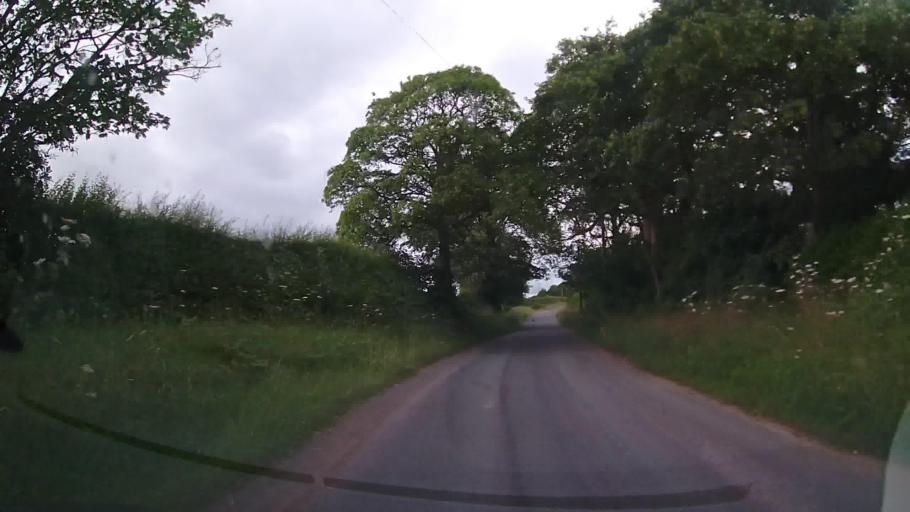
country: GB
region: England
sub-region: Shropshire
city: Whitchurch
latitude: 52.9286
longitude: -2.7316
